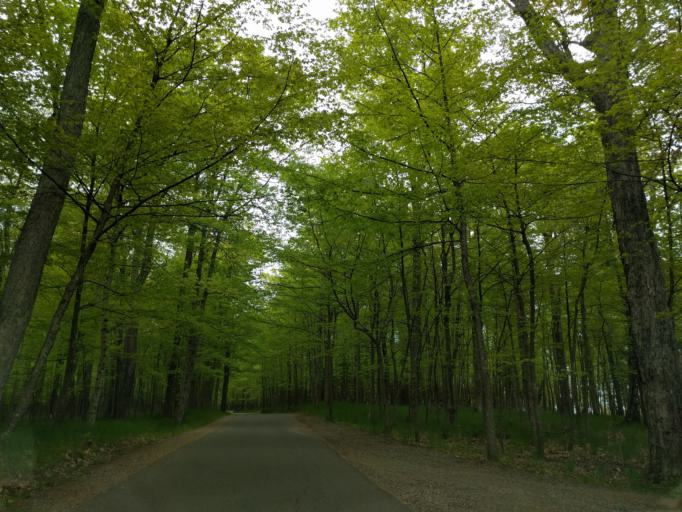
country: US
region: Michigan
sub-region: Marquette County
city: Marquette
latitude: 46.5829
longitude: -87.3804
